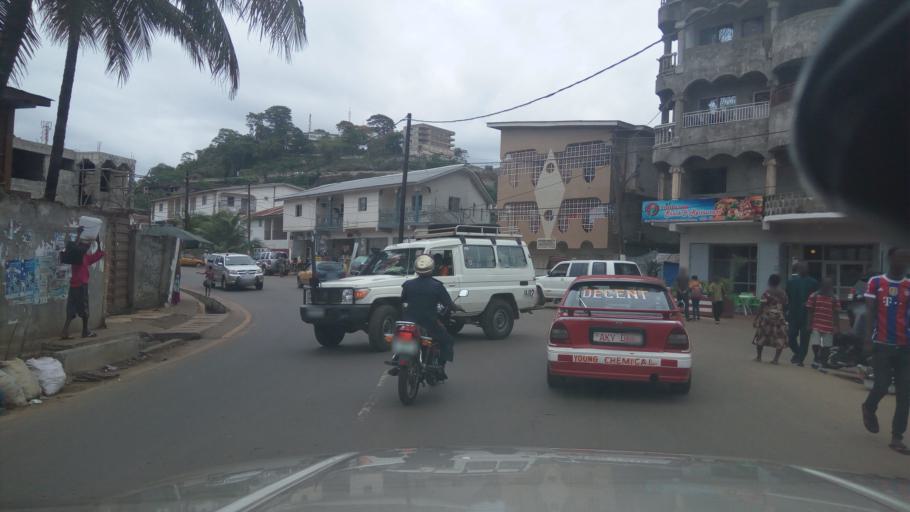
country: SL
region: Western Area
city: Freetown
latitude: 8.4860
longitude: -13.2689
